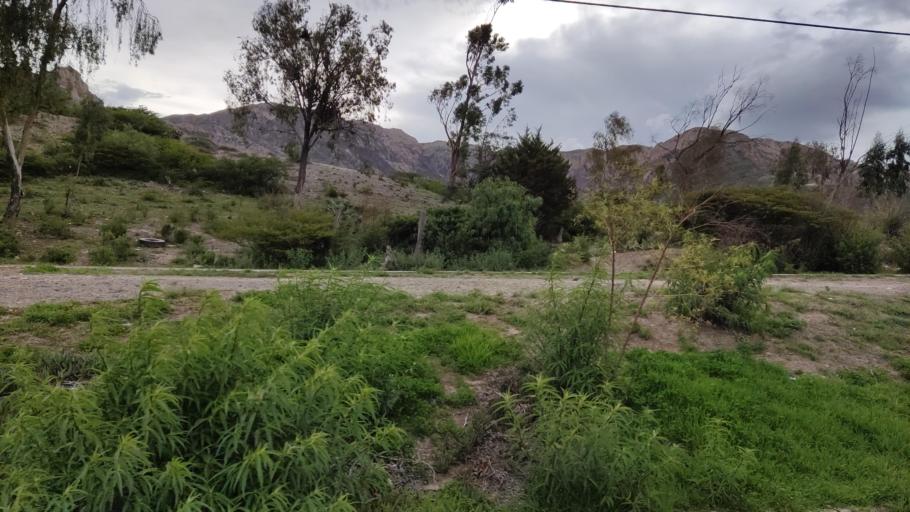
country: BO
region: La Paz
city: La Paz
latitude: -16.5849
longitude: -68.0776
